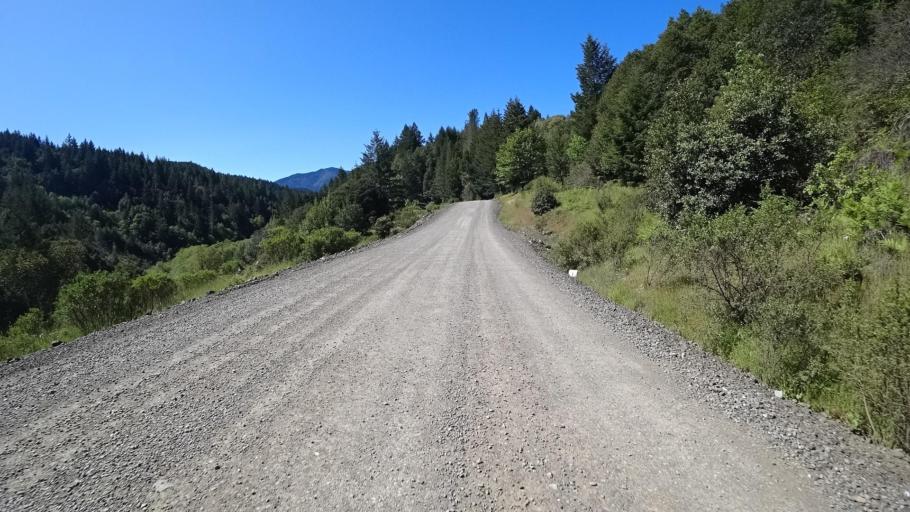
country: US
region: California
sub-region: Humboldt County
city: Rio Dell
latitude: 40.2264
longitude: -124.1110
